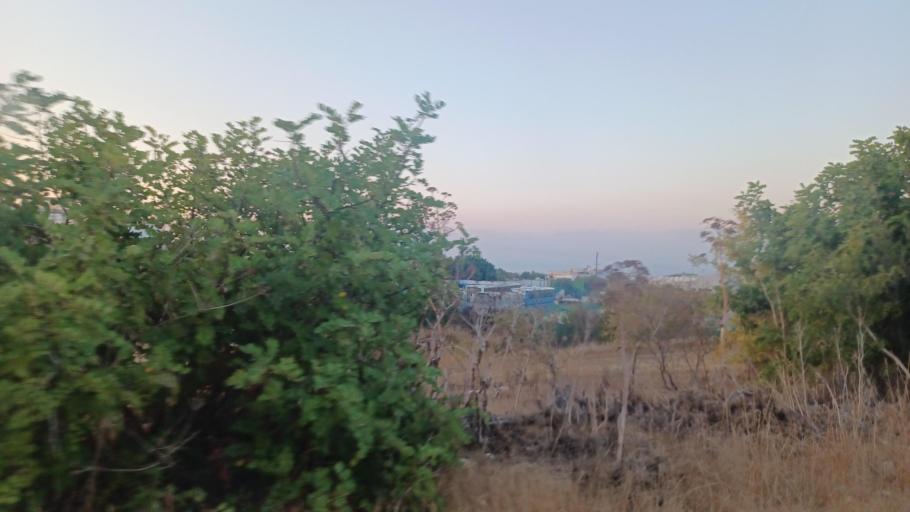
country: CY
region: Pafos
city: Mesogi
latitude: 34.8122
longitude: 32.4425
